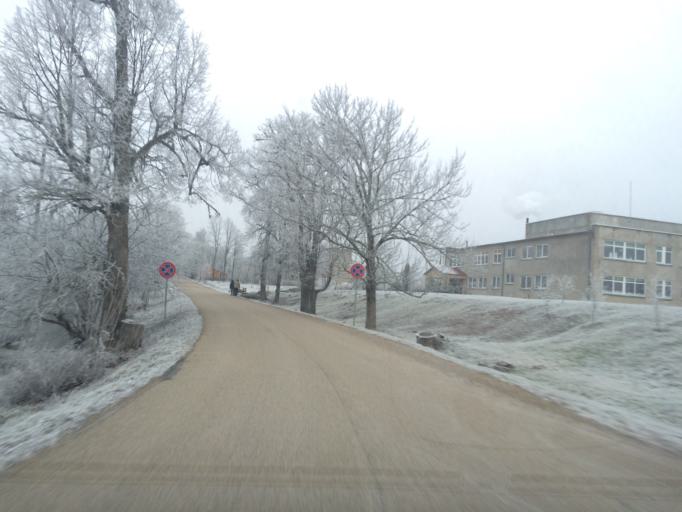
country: LV
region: Ludzas Rajons
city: Ludza
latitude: 56.6284
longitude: 27.5153
